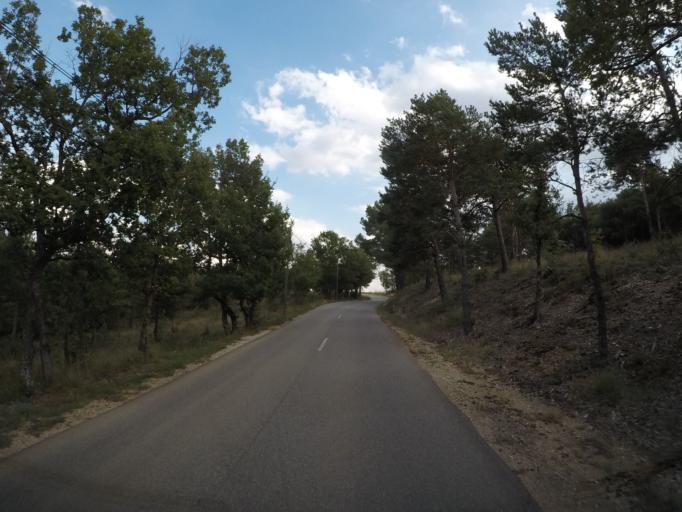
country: FR
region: Provence-Alpes-Cote d'Azur
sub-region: Departement des Alpes-de-Haute-Provence
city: Valensole
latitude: 43.8317
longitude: 6.0291
